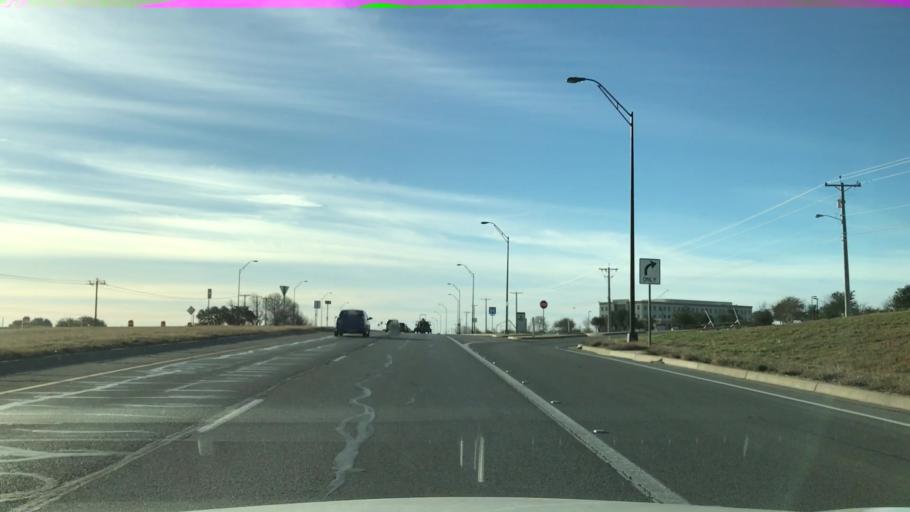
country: US
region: Texas
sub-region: Williamson County
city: Round Rock
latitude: 30.5698
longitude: -97.6498
